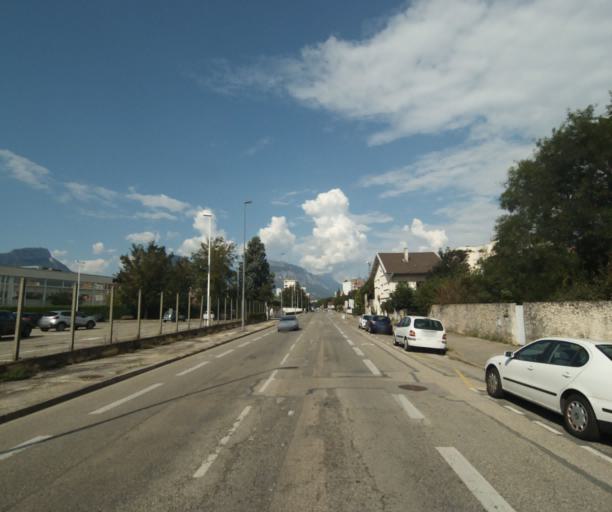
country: FR
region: Rhone-Alpes
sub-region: Departement de l'Isere
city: Grenoble
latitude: 45.1659
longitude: 5.7194
